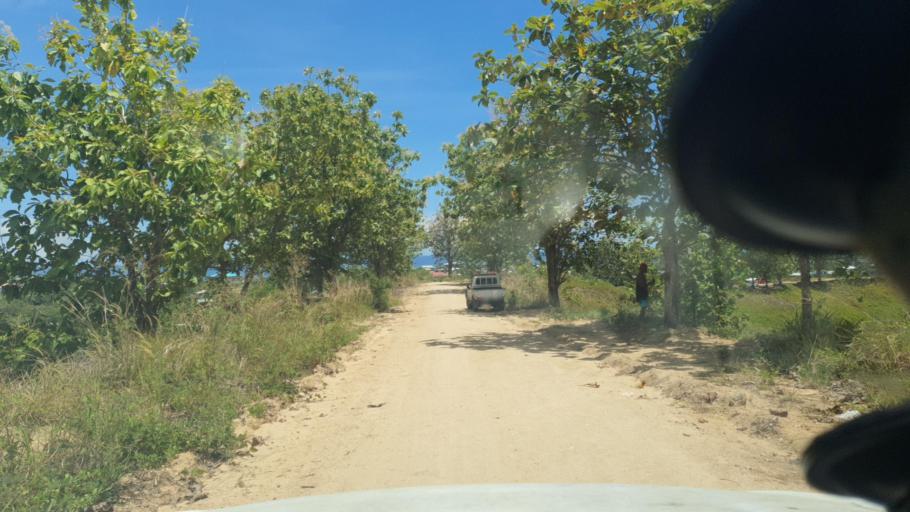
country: SB
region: Guadalcanal
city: Honiara
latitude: -9.4382
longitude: 159.9264
